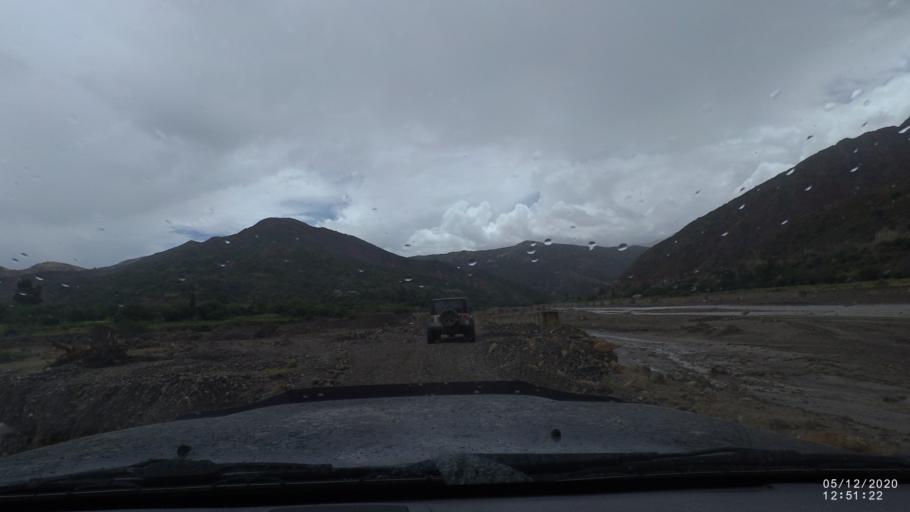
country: BO
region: Cochabamba
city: Sipe Sipe
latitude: -17.5509
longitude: -66.4402
